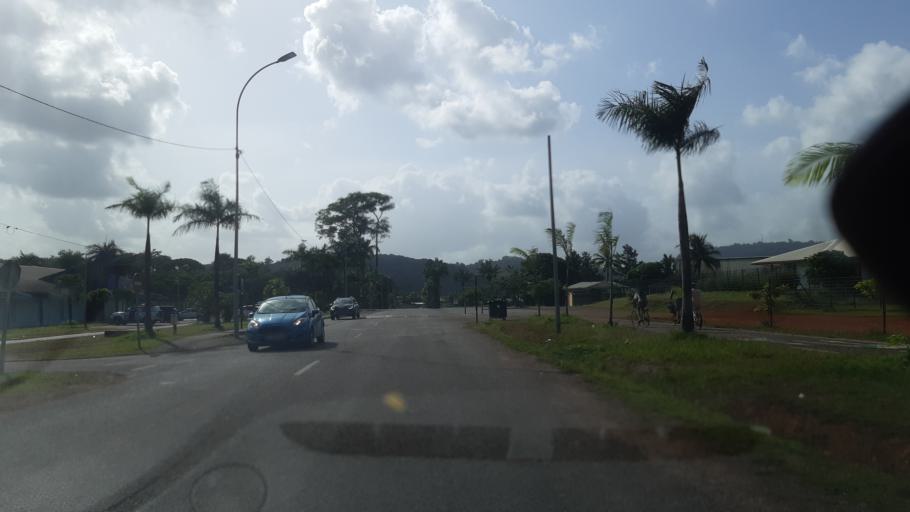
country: GF
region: Guyane
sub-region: Guyane
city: Matoury
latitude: 4.8456
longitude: -52.3265
